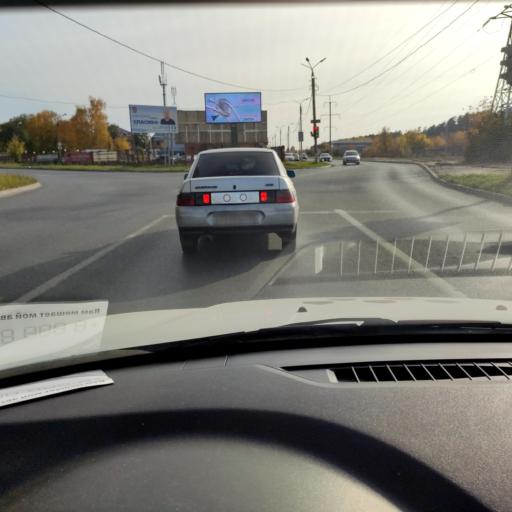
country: RU
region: Samara
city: Tol'yatti
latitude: 53.5248
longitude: 49.3962
